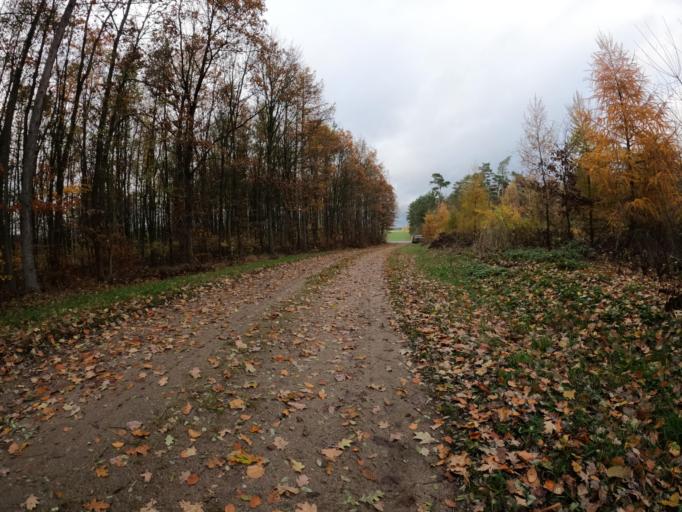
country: PL
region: West Pomeranian Voivodeship
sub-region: Powiat walecki
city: Tuczno
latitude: 53.2331
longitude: 16.2535
